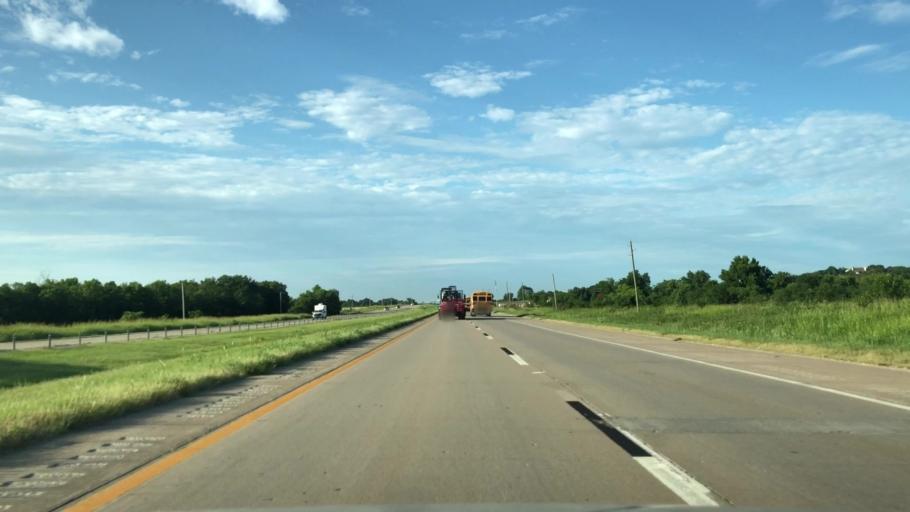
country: US
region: Oklahoma
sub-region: Osage County
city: Skiatook
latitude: 36.4707
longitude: -95.9207
